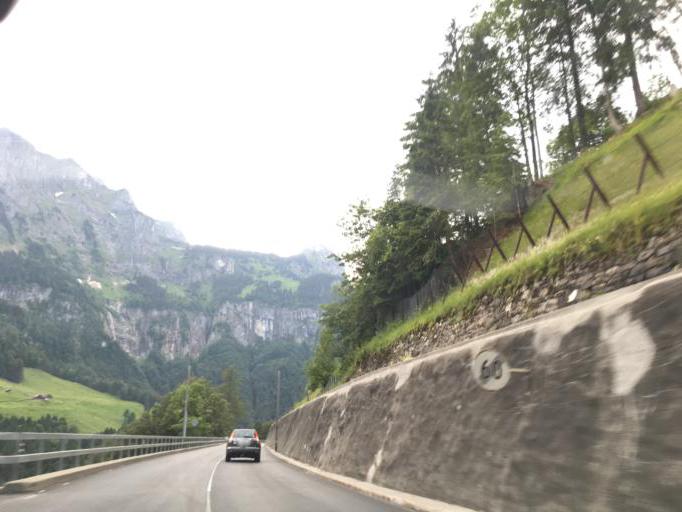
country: CH
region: Obwalden
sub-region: Obwalden
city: Engelberg
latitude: 46.8244
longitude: 8.3849
